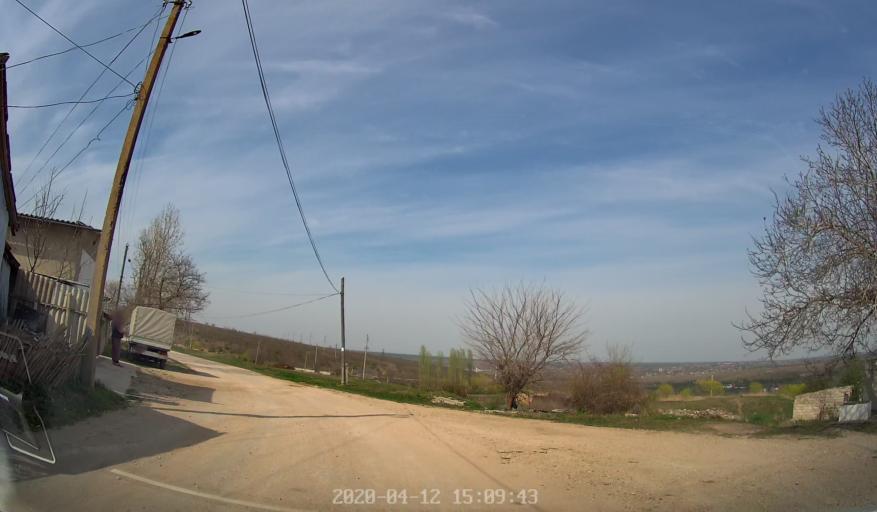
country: MD
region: Telenesti
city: Cocieri
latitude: 47.3212
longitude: 29.0685
